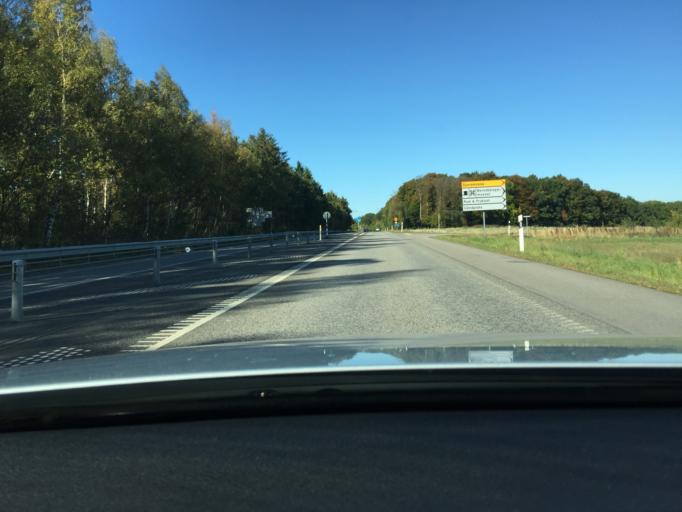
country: DK
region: Capital Region
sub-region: Helsingor Kommune
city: Hellebaek
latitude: 56.1222
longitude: 12.6208
